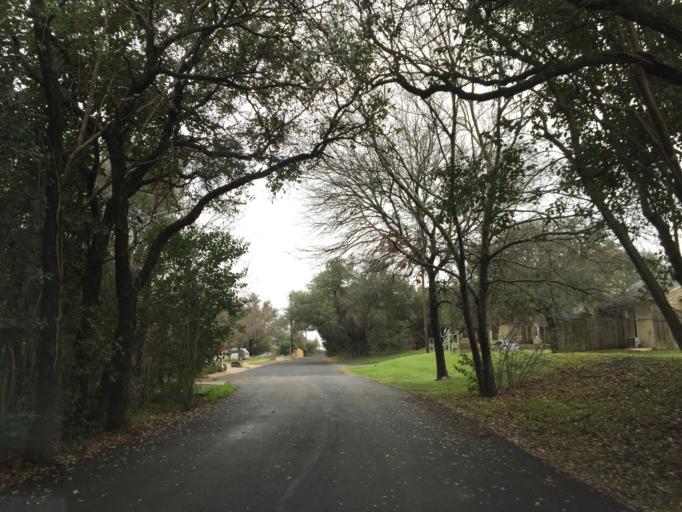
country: US
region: Texas
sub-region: Williamson County
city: Jollyville
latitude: 30.4164
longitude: -97.7354
